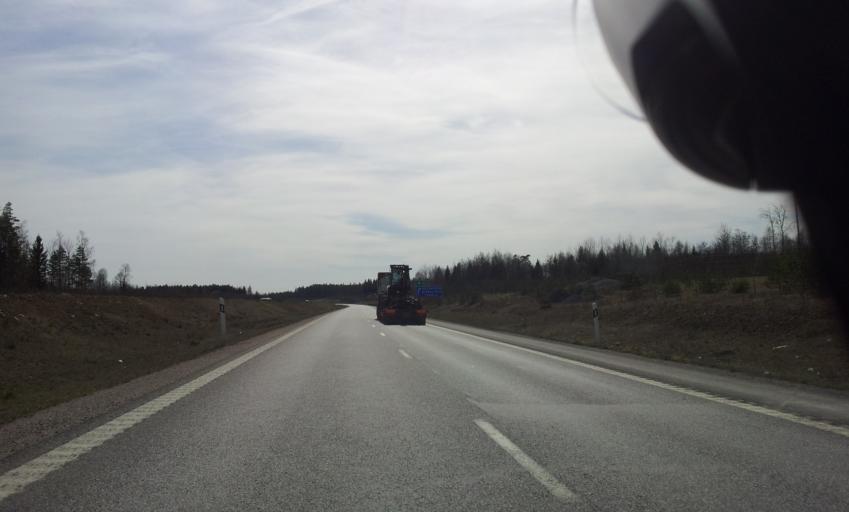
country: SE
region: Uppsala
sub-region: Osthammars Kommun
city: Bjorklinge
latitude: 60.0292
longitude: 17.6278
